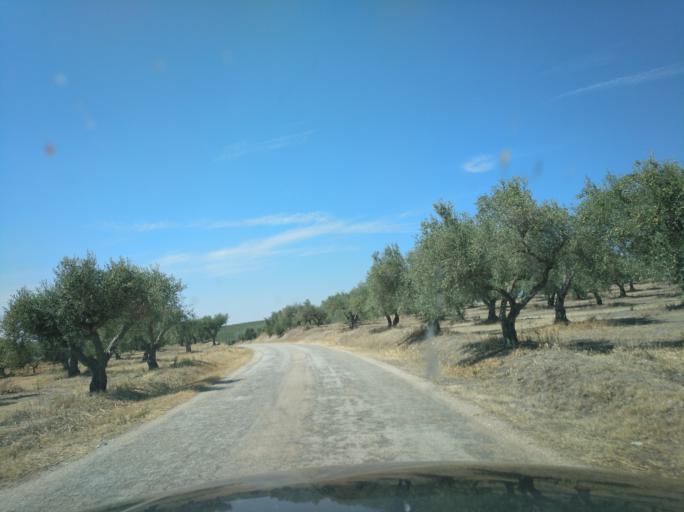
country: PT
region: Portalegre
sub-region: Campo Maior
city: Campo Maior
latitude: 38.9854
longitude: -7.1009
